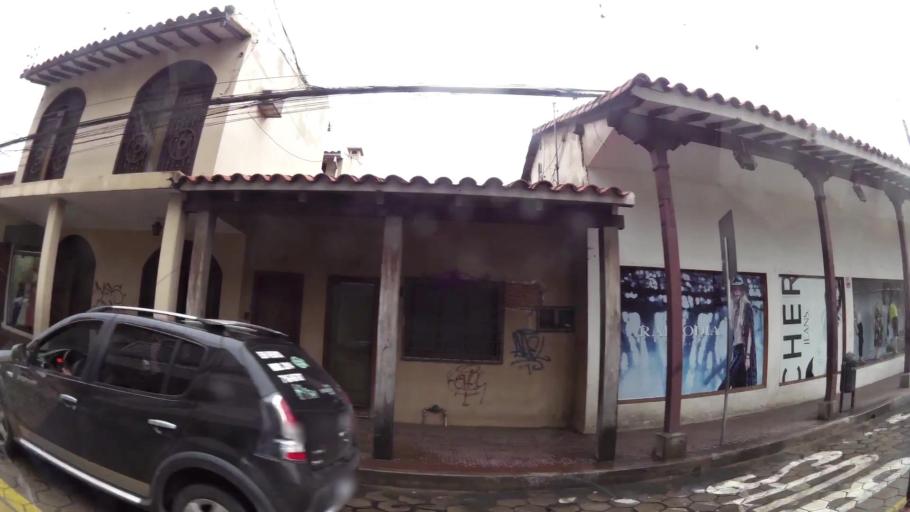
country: BO
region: Santa Cruz
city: Santa Cruz de la Sierra
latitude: -17.7873
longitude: -63.1836
